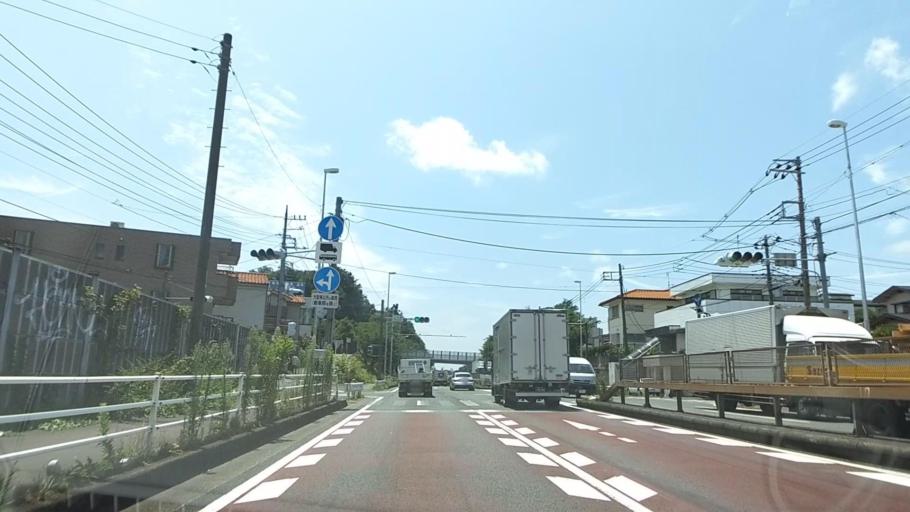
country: JP
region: Kanagawa
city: Zama
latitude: 35.4673
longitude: 139.4072
